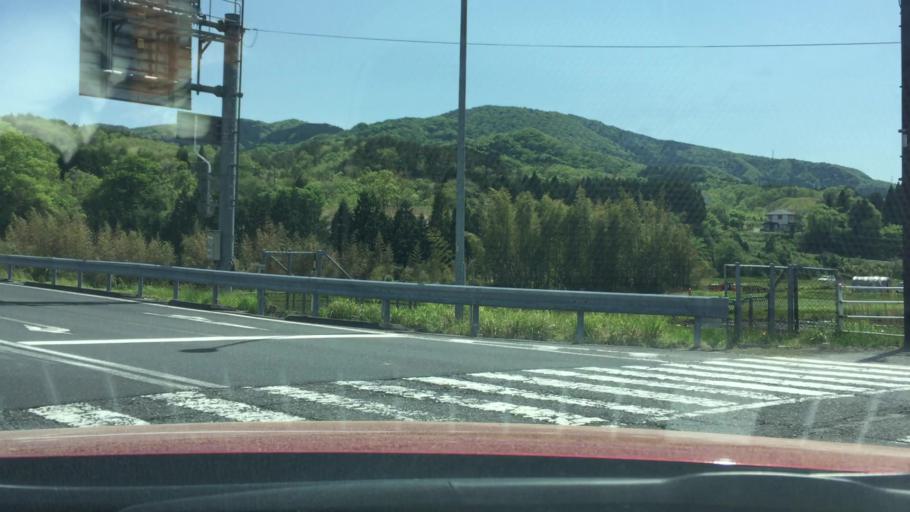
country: JP
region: Tottori
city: Kurayoshi
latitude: 35.2766
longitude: 133.6222
